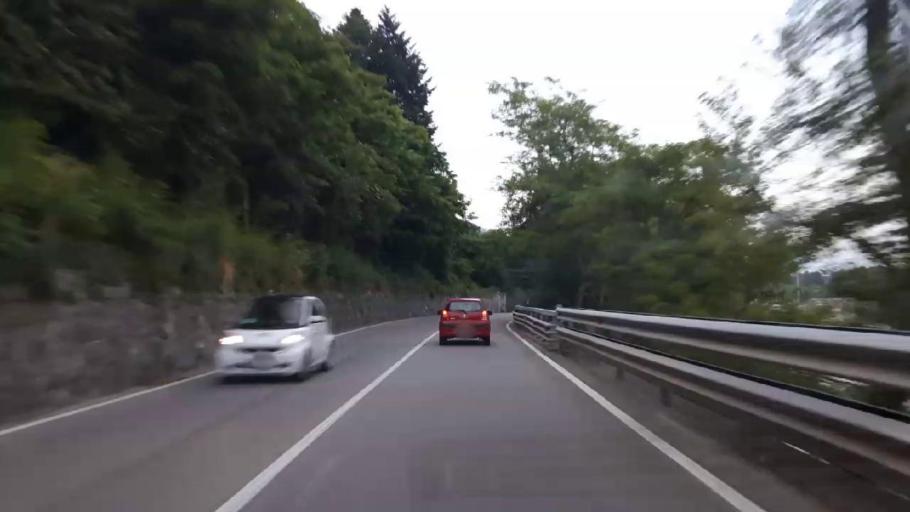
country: IT
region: Piedmont
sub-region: Provincia di Novara
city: Massino Visconti
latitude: 45.8116
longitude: 8.5438
